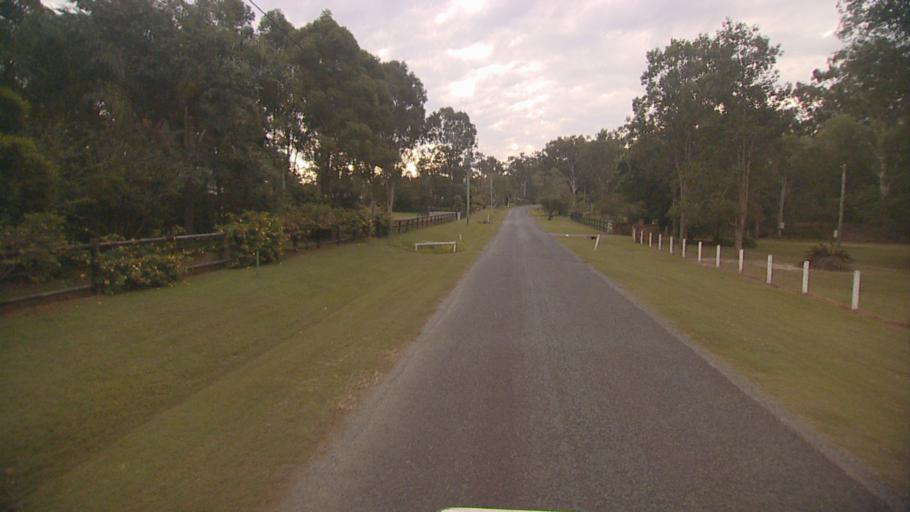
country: AU
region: Queensland
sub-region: Logan
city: Chambers Flat
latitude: -27.7920
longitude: 153.1114
